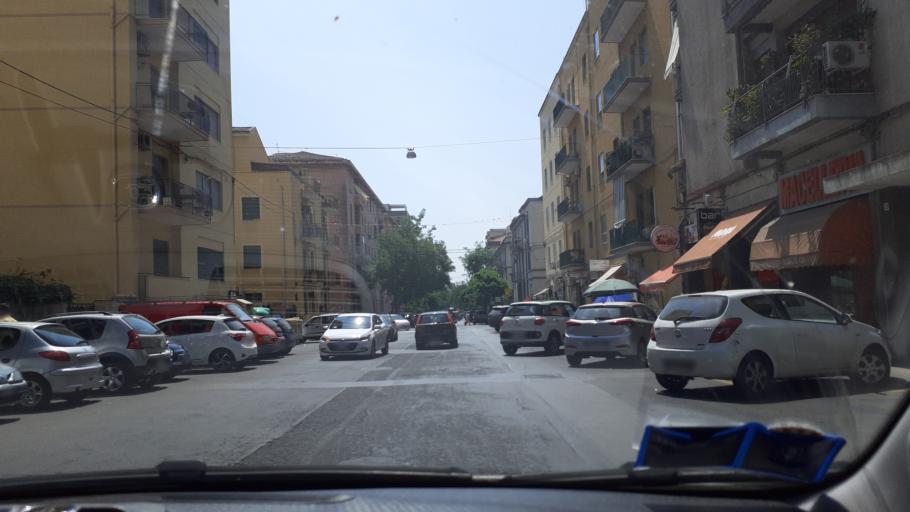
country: IT
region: Sicily
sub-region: Catania
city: Catania
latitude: 37.5135
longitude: 15.0743
